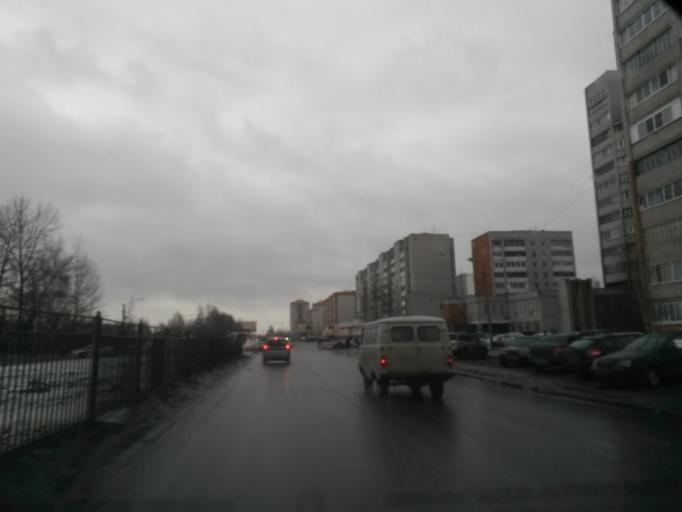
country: RU
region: Jaroslavl
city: Yaroslavl
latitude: 57.6449
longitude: 39.9555
